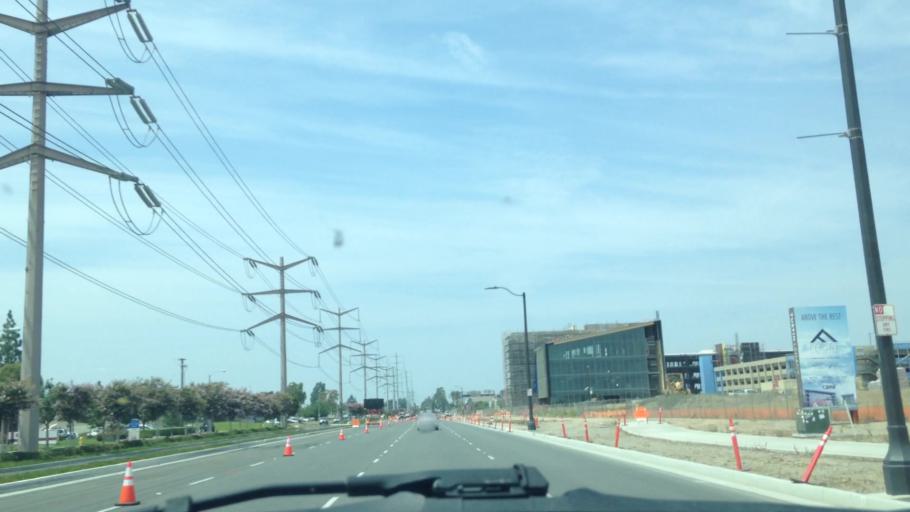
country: US
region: California
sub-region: Orange County
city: Irvine
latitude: 33.7014
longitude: -117.8370
